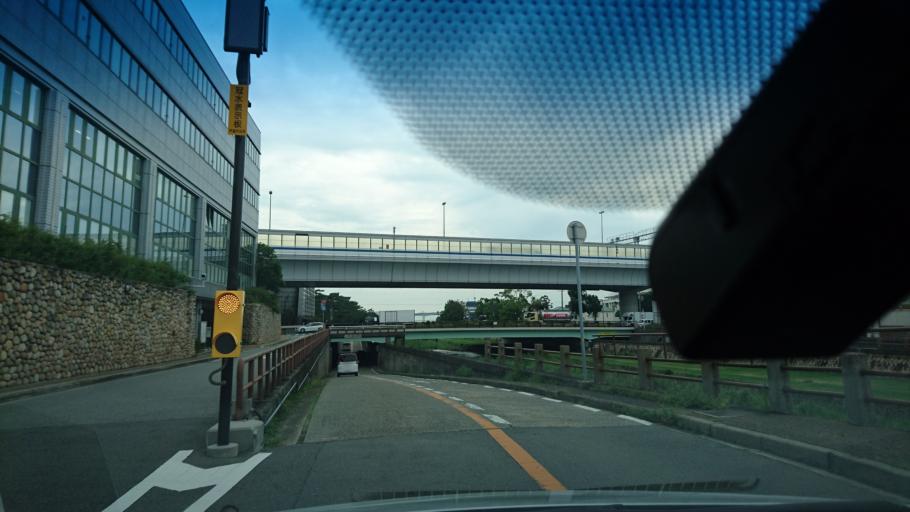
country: JP
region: Hyogo
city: Ashiya
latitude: 34.7268
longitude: 135.3038
